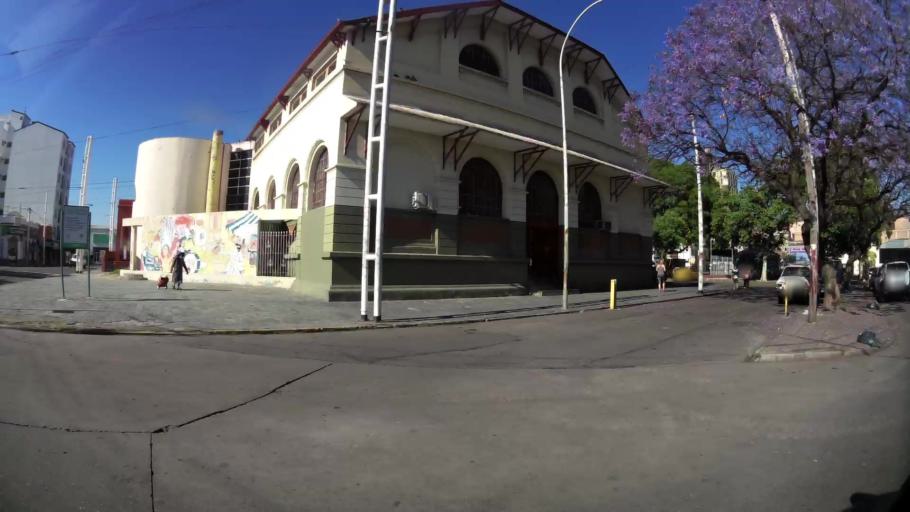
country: AR
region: Cordoba
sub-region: Departamento de Capital
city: Cordoba
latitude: -31.4231
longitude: -64.1477
